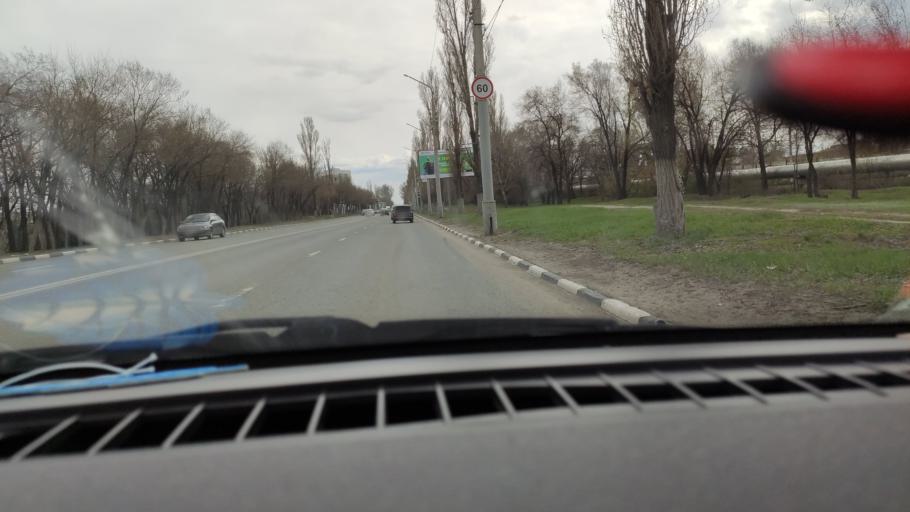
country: RU
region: Saratov
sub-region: Saratovskiy Rayon
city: Saratov
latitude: 51.5748
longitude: 45.9897
